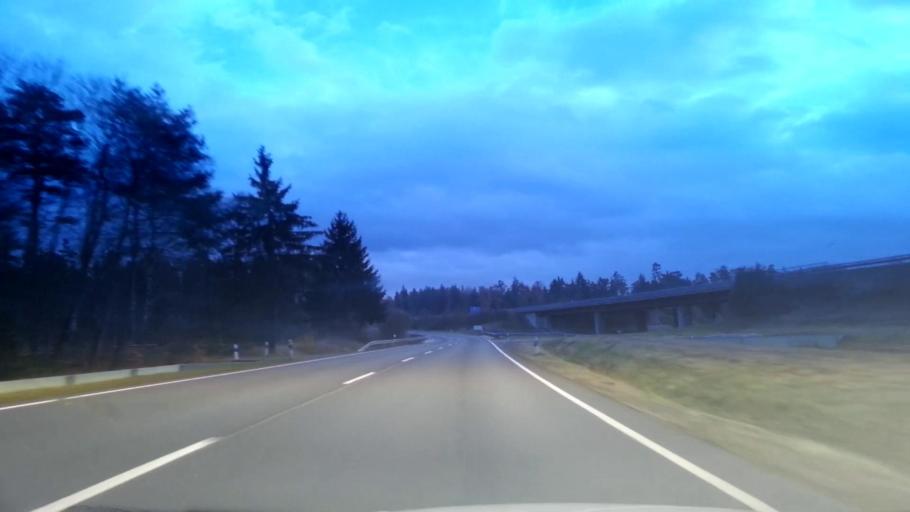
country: DE
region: Bavaria
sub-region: Upper Palatinate
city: Pechbrunn
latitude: 49.9577
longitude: 12.1931
